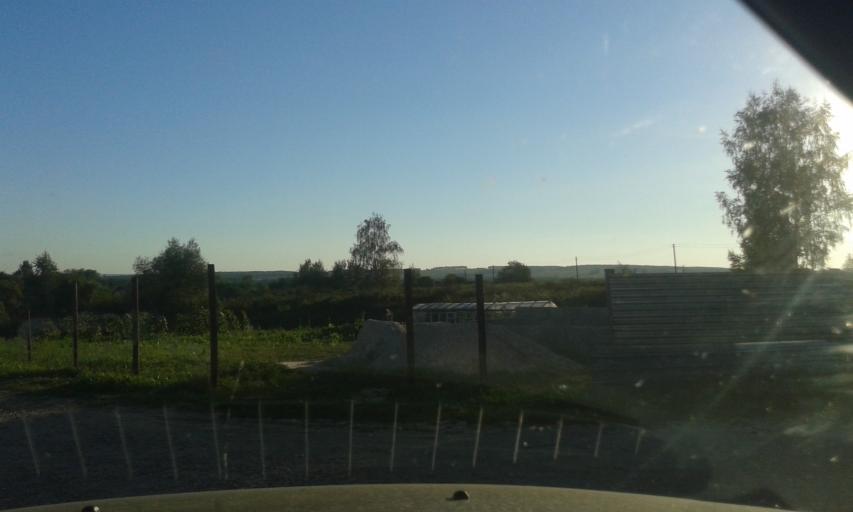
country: RU
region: Tula
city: Dubna
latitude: 54.1376
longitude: 37.1524
